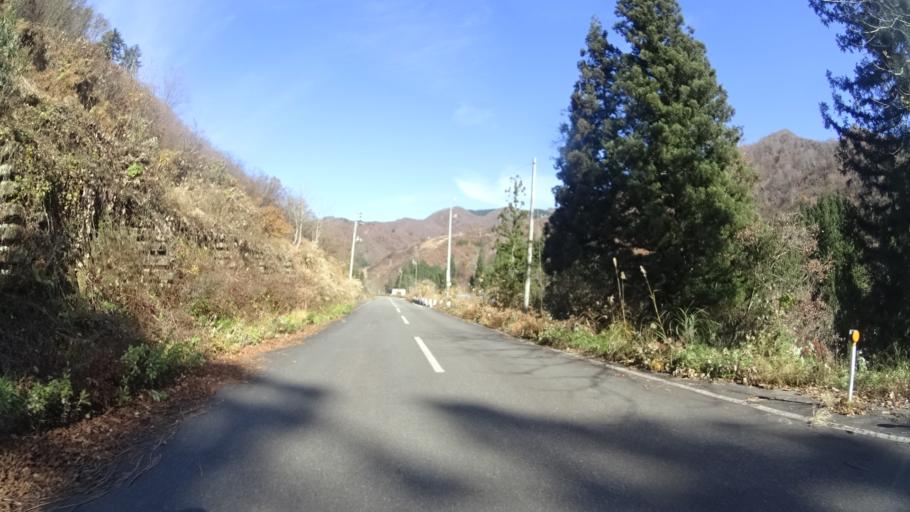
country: JP
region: Niigata
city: Muikamachi
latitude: 37.1870
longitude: 139.0812
